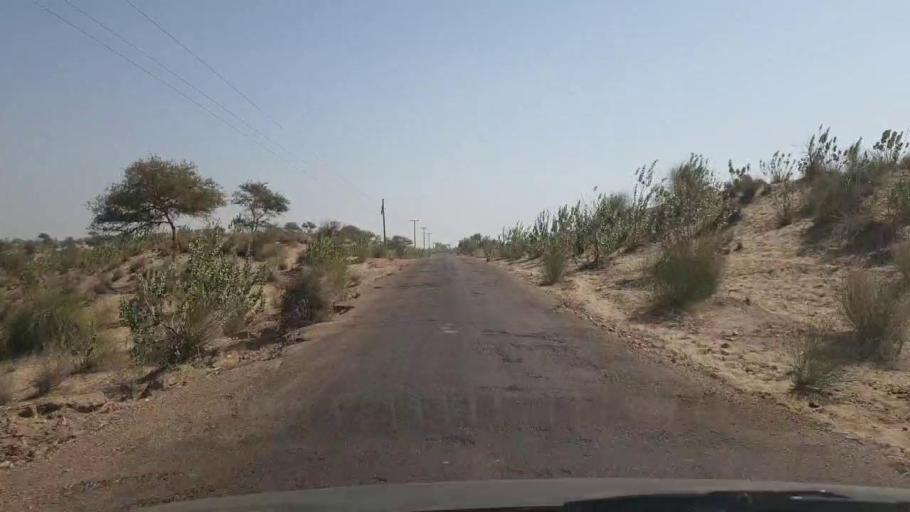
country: PK
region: Sindh
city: Chor
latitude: 25.5951
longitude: 69.9688
